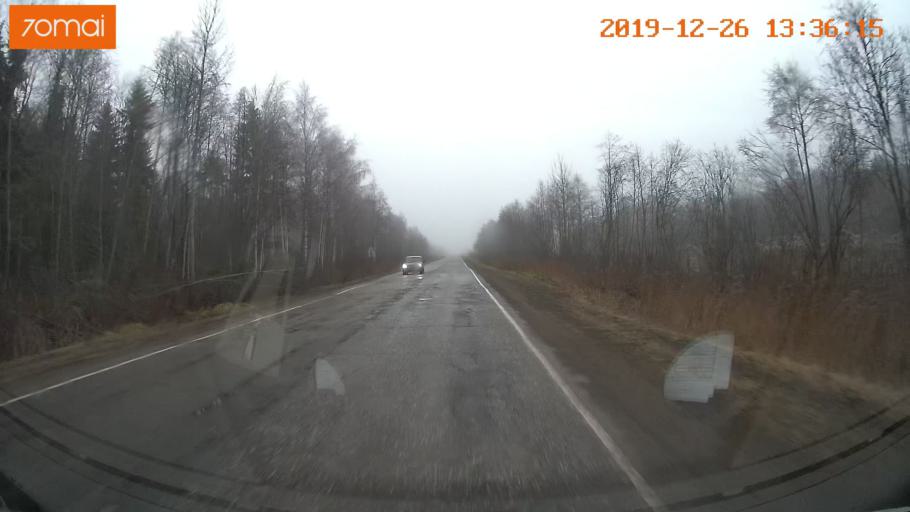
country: RU
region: Vologda
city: Sheksna
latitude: 58.7847
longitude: 38.3523
